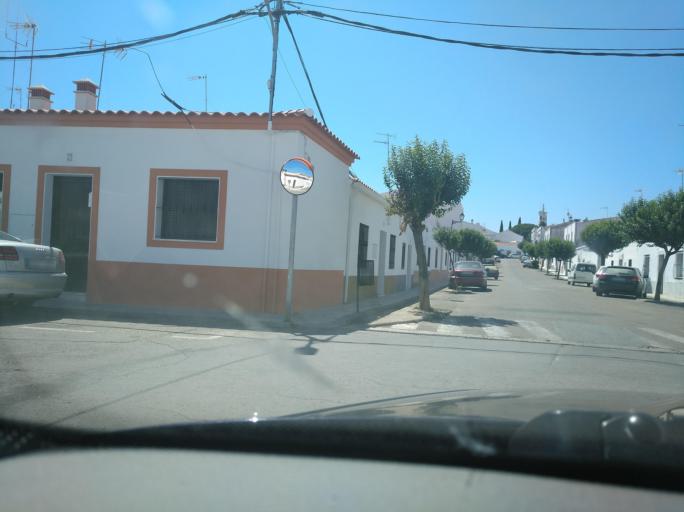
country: ES
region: Extremadura
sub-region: Provincia de Badajoz
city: Olivenza
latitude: 38.6802
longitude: -7.1015
